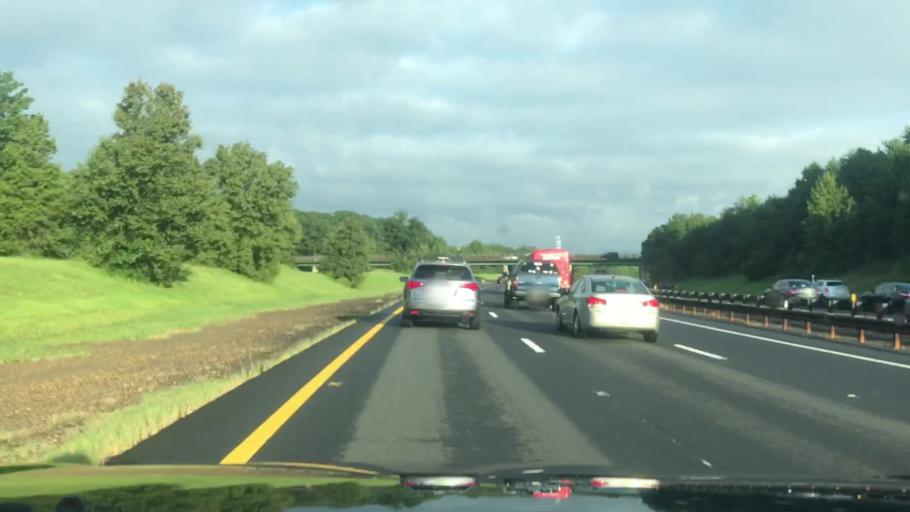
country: US
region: New Jersey
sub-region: Monmouth County
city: Matawan
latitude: 40.4300
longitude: -74.2424
